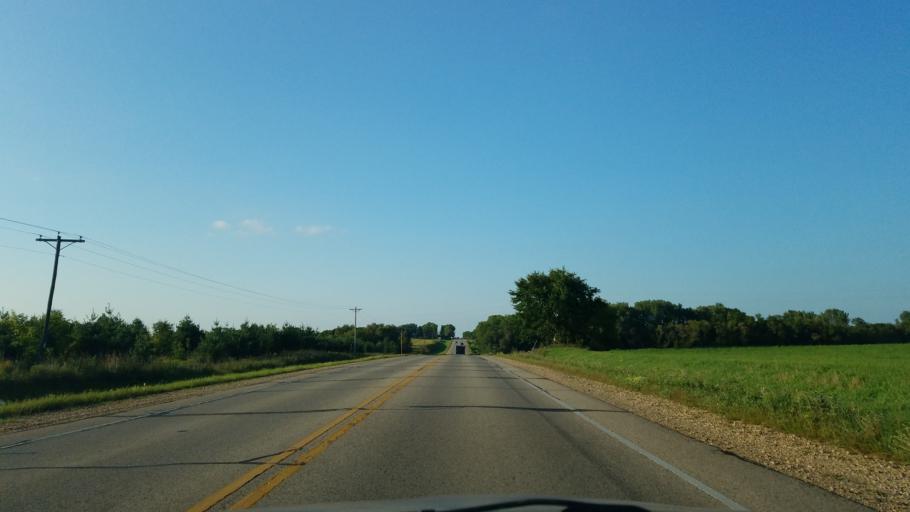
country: US
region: Wisconsin
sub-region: Saint Croix County
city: New Richmond
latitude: 45.0539
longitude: -92.5374
